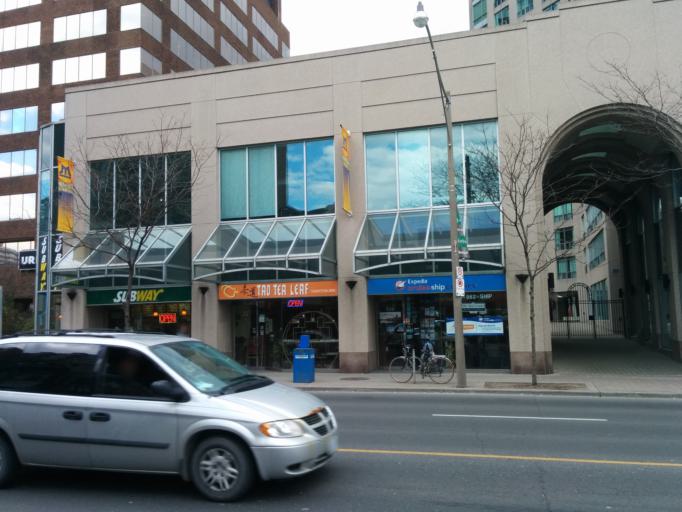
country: CA
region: Ontario
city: Toronto
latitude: 43.6742
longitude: -79.3888
